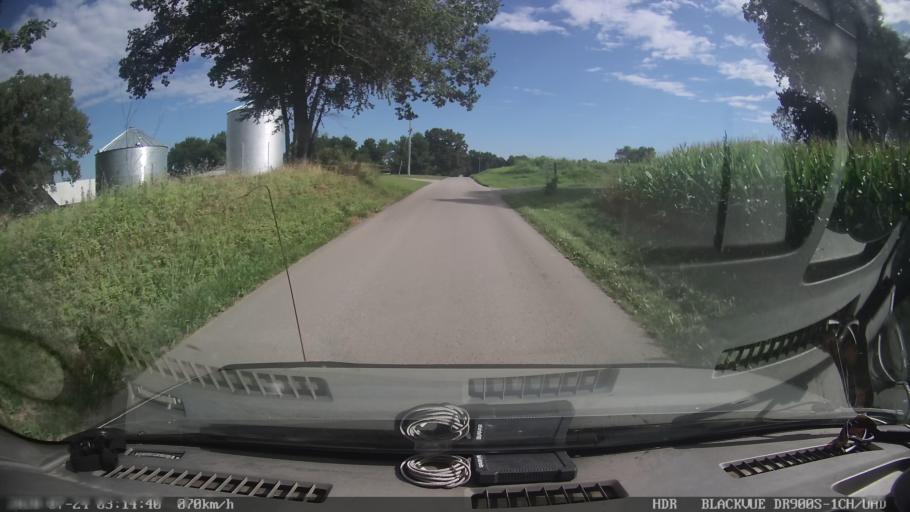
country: US
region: Kentucky
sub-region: Todd County
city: Guthrie
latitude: 36.6885
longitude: -87.1709
